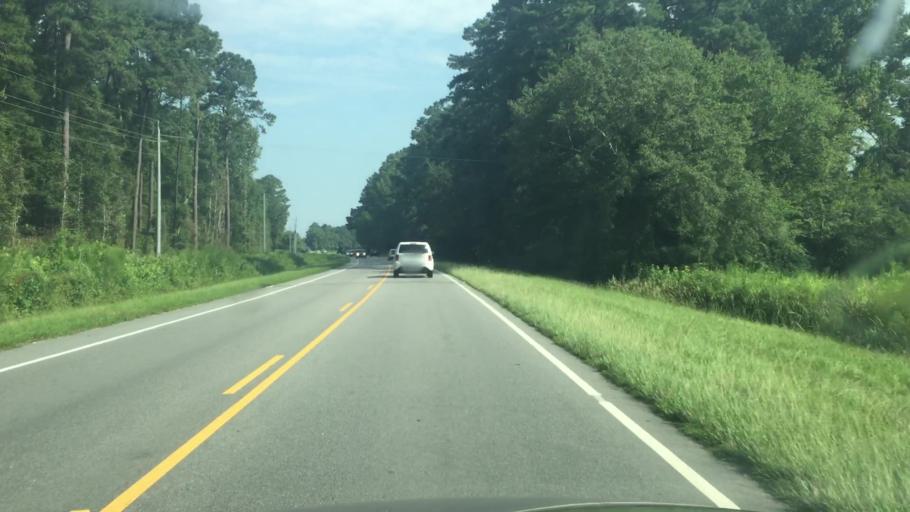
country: US
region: North Carolina
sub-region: Columbus County
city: Chadbourn
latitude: 34.3443
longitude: -78.8272
